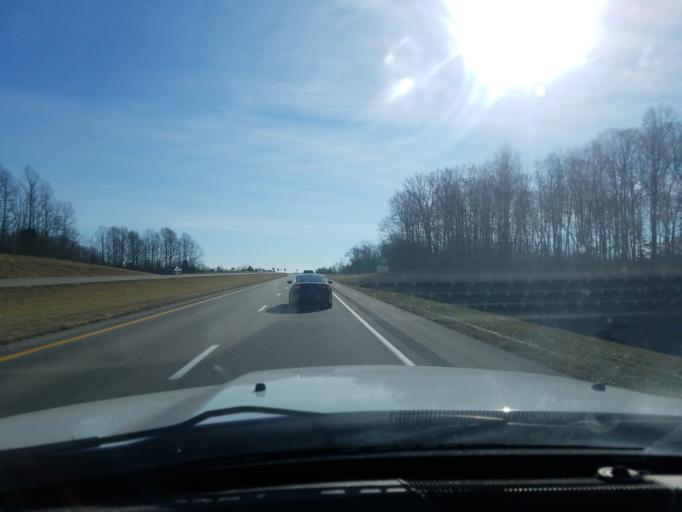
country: US
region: Ohio
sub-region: Adams County
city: Winchester
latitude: 38.9422
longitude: -83.6734
